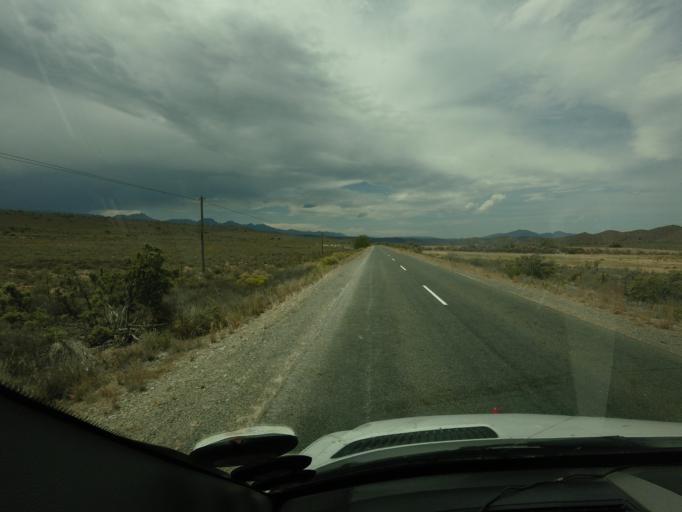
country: ZA
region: Western Cape
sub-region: Eden District Municipality
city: Ladismith
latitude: -33.6020
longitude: 21.0857
